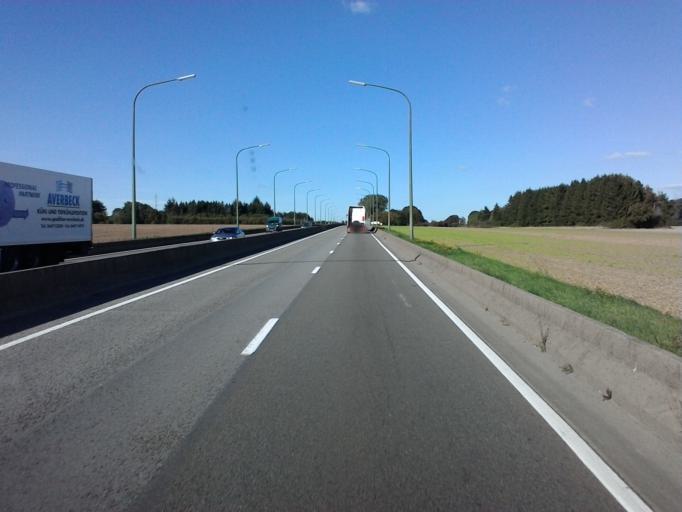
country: BE
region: Wallonia
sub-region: Province du Luxembourg
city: Arlon
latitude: 49.6403
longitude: 5.8158
